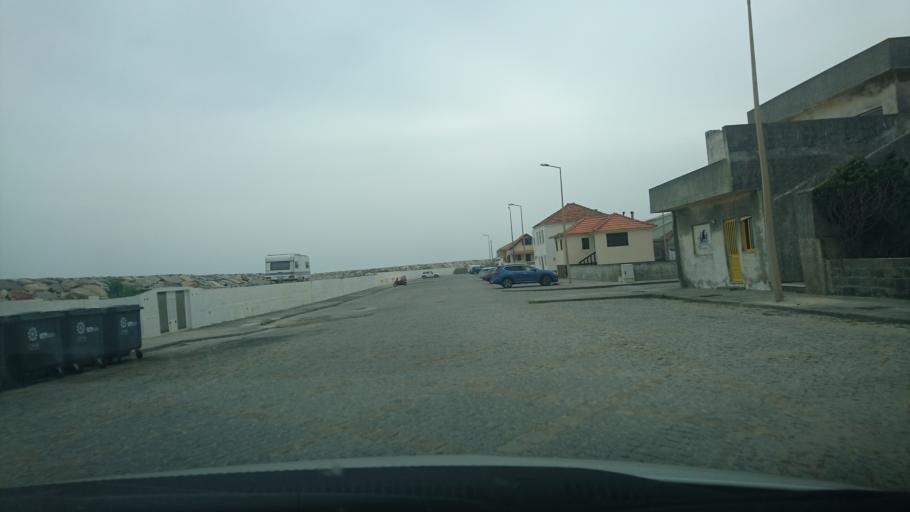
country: PT
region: Aveiro
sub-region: Ovar
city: Esmoriz
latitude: 40.9529
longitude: -8.6561
